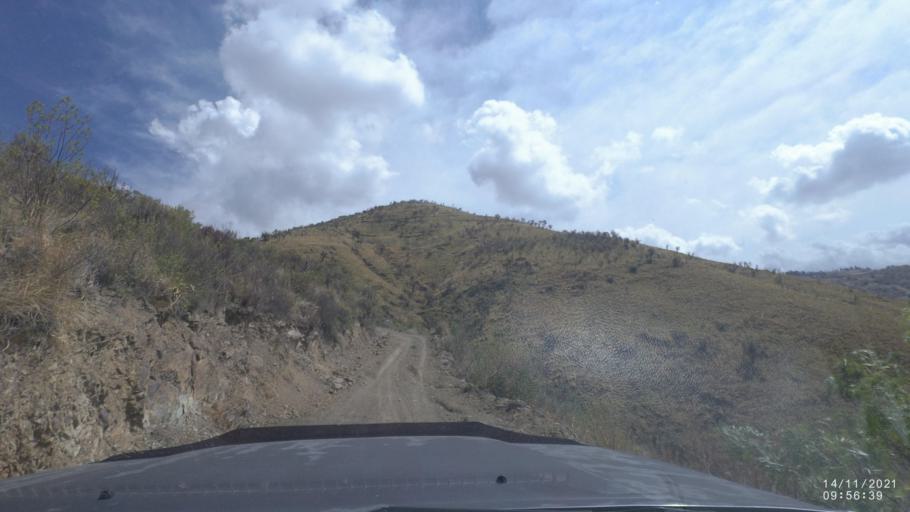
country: BO
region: Cochabamba
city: Cochabamba
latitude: -17.3566
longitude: -66.0877
